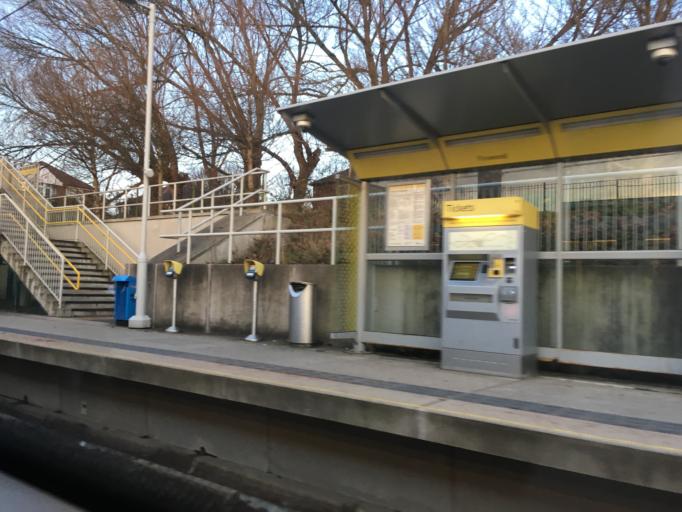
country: GB
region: England
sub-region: Manchester
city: Chorlton cum Hardy
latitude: 53.4512
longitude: -2.2777
